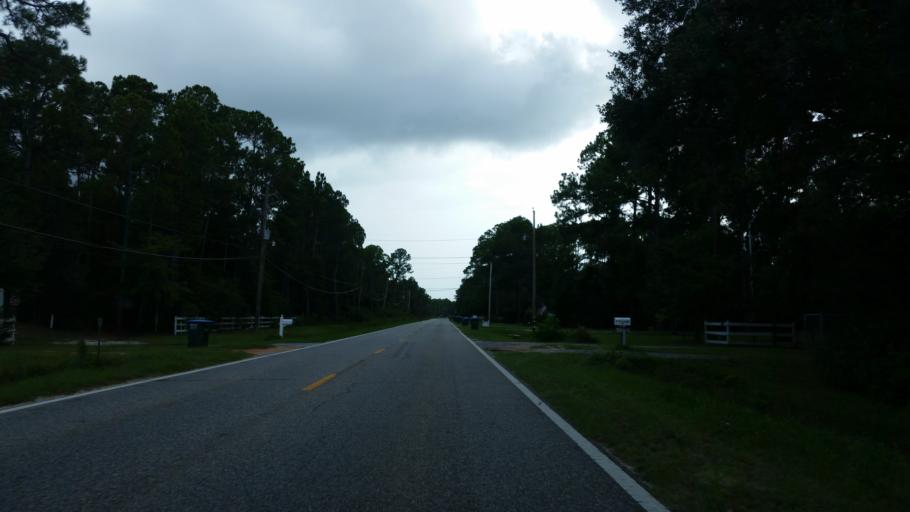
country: US
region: Florida
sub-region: Santa Rosa County
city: Holley
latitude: 30.4391
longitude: -86.9542
